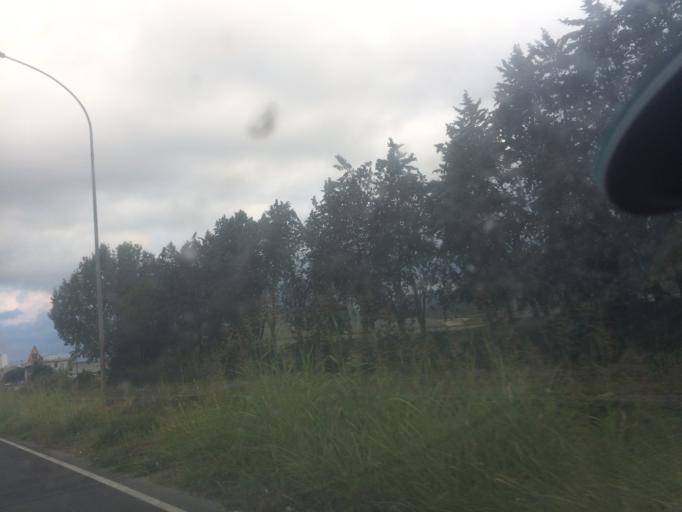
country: IT
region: Tuscany
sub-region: Provincia di Massa-Carrara
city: Carrara
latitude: 44.0375
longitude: 10.0847
